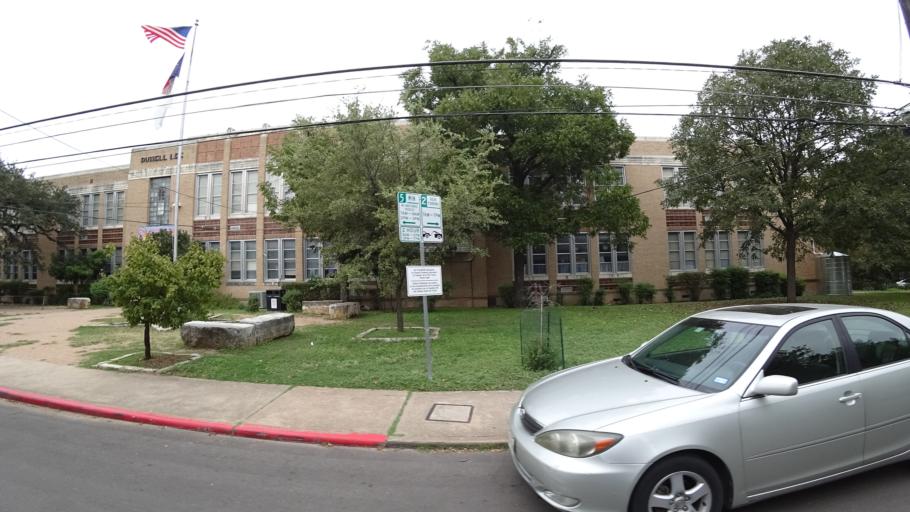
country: US
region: Texas
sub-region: Travis County
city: Austin
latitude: 30.2934
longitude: -97.7270
